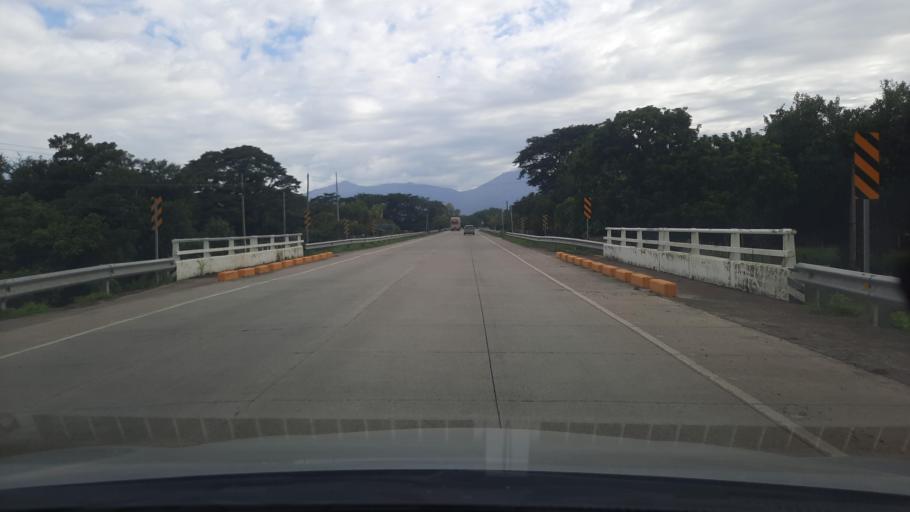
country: NI
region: Chinandega
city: Somotillo
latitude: 12.8454
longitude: -86.8788
